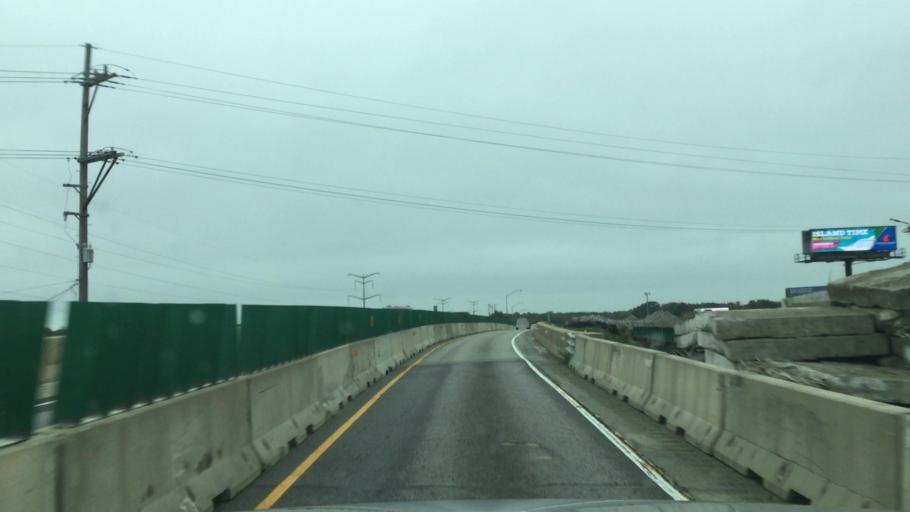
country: US
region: Illinois
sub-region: Lake County
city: Deerfield
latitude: 42.1488
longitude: -87.8398
